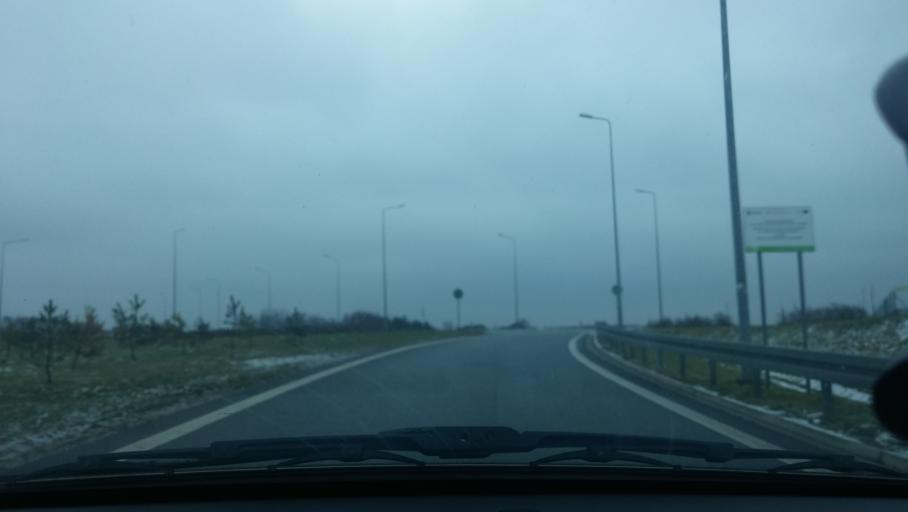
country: PL
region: Masovian Voivodeship
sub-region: Powiat minski
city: Jakubow
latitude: 52.2027
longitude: 21.7164
